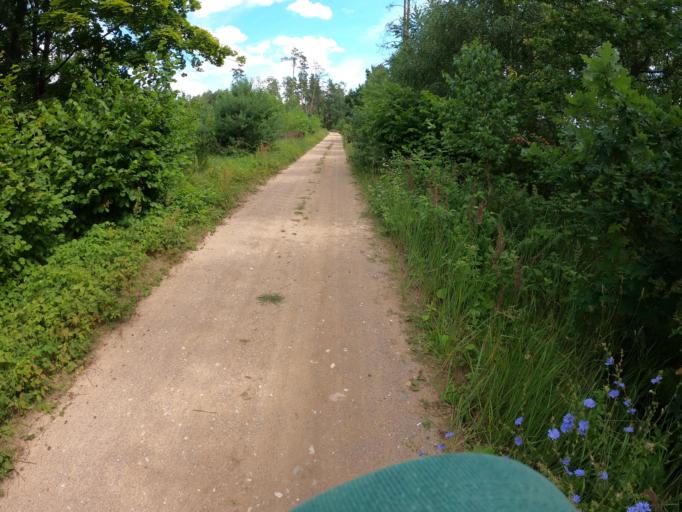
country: LT
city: Jieznas
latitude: 54.6608
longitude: 24.1260
